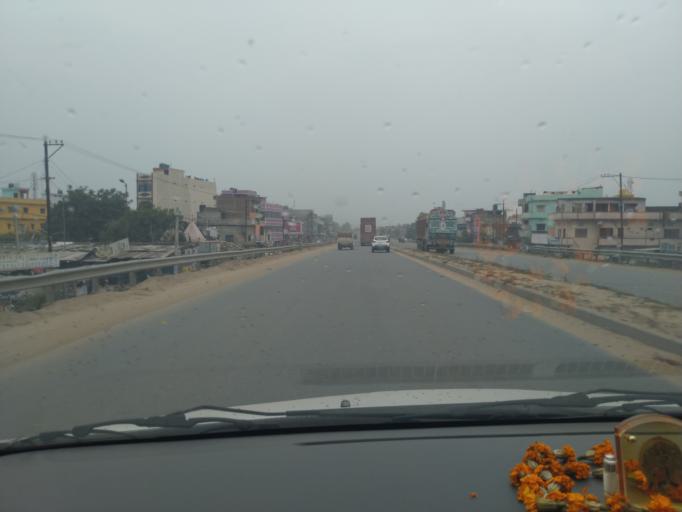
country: IN
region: Bihar
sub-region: Rohtas
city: Dehri
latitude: 24.9080
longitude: 84.1843
